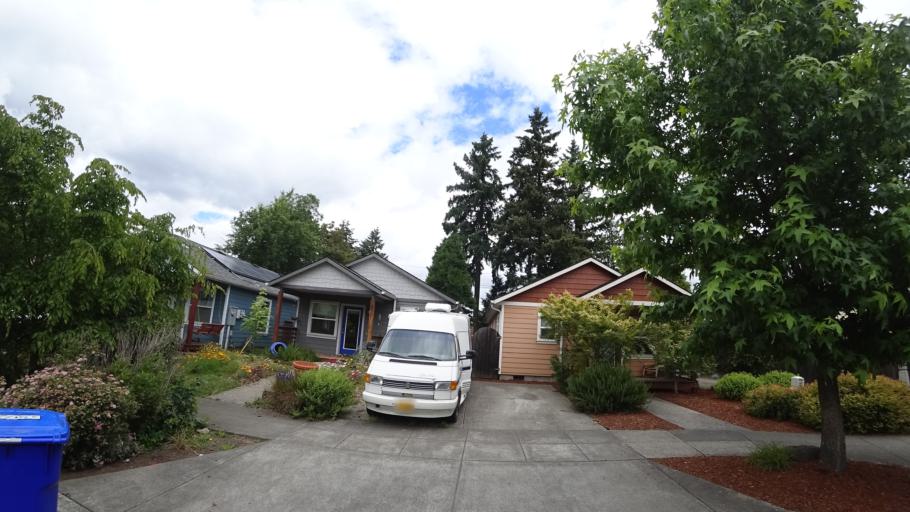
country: US
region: Oregon
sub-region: Multnomah County
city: Lents
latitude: 45.5621
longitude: -122.5970
